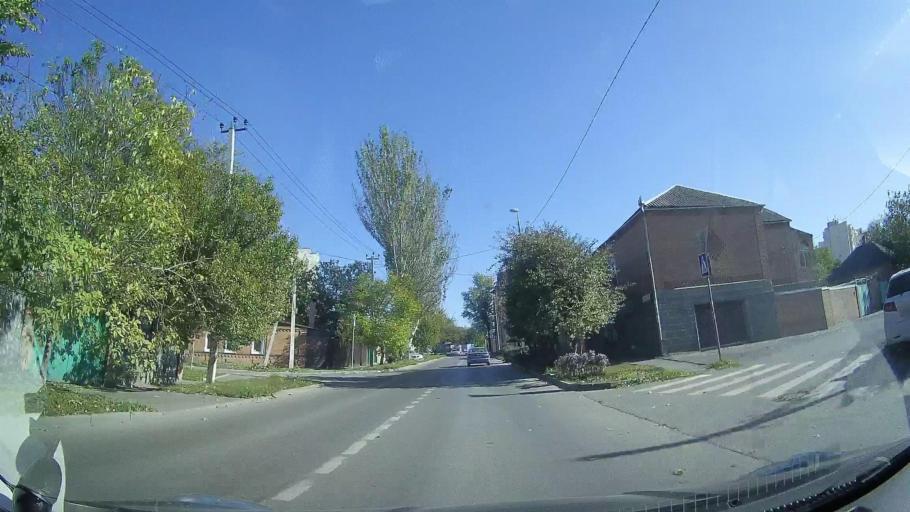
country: RU
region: Rostov
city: Rostov-na-Donu
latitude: 47.2399
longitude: 39.6808
